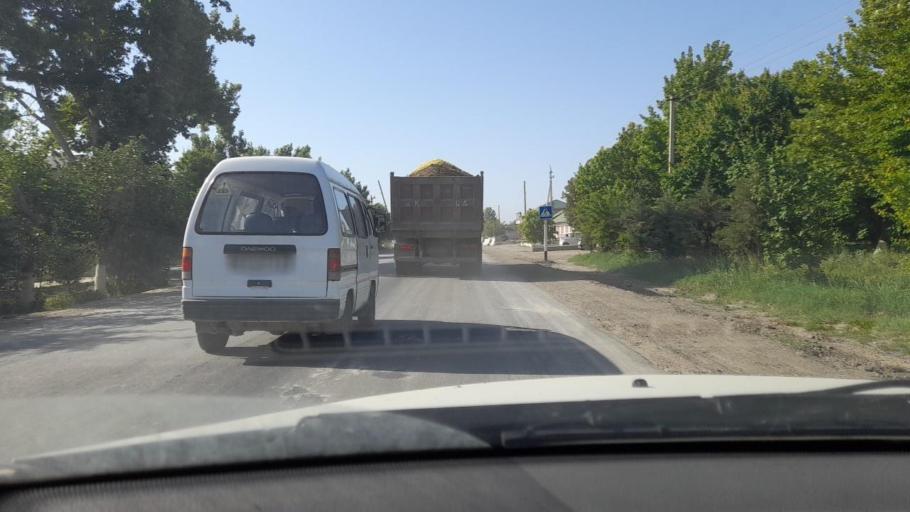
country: UZ
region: Bukhara
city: Romiton
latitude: 40.0487
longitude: 64.3286
